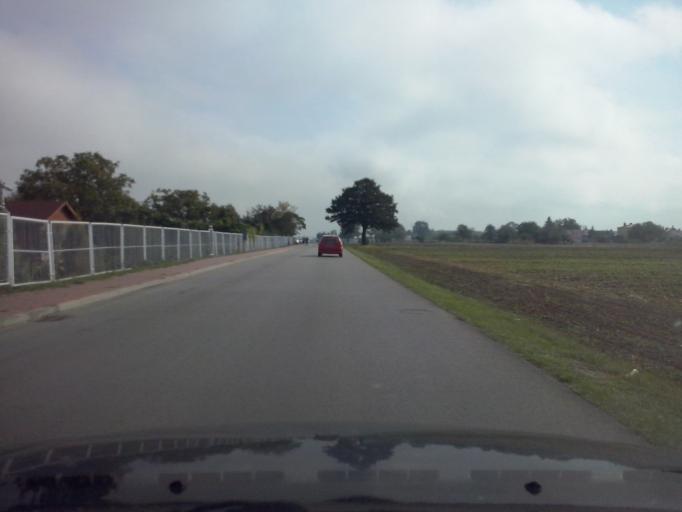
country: PL
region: Subcarpathian Voivodeship
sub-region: Powiat mielecki
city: Mielec
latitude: 50.3166
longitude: 21.4366
